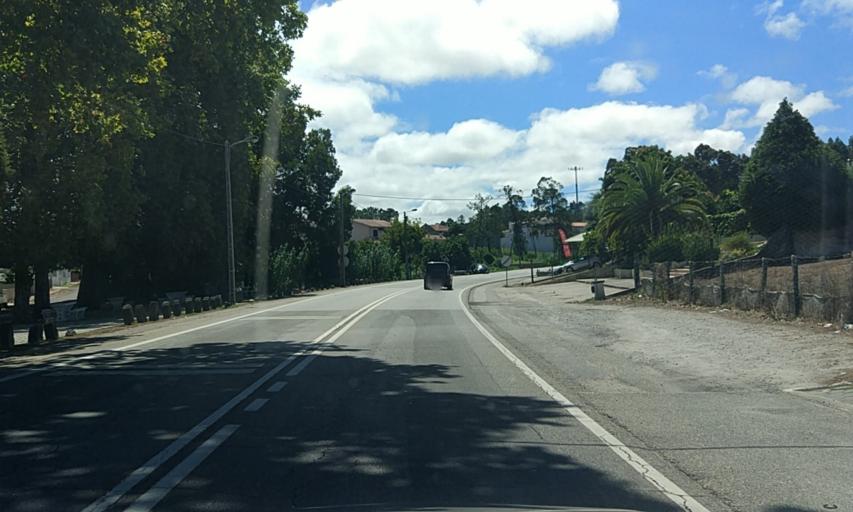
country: PT
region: Aveiro
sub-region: Vagos
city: Vagos
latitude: 40.5100
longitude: -8.6772
